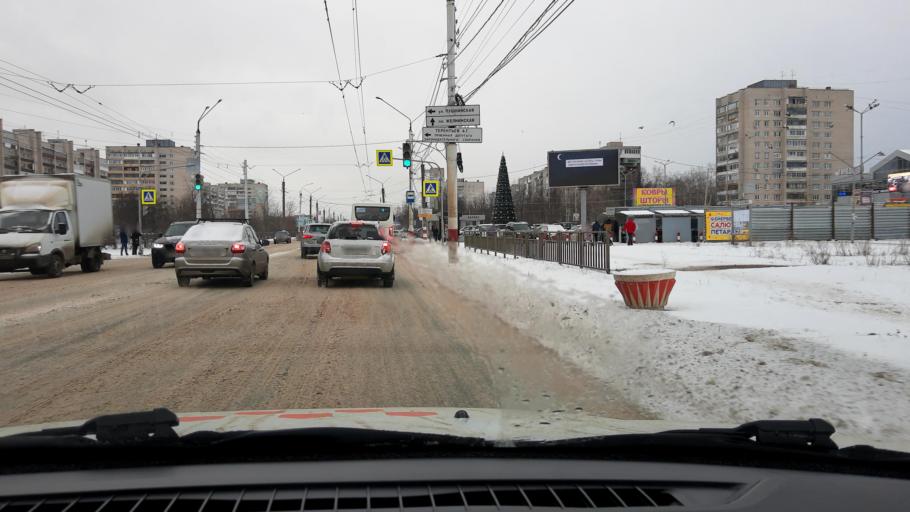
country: RU
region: Nizjnij Novgorod
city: Dzerzhinsk
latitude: 56.2269
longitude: 43.4003
